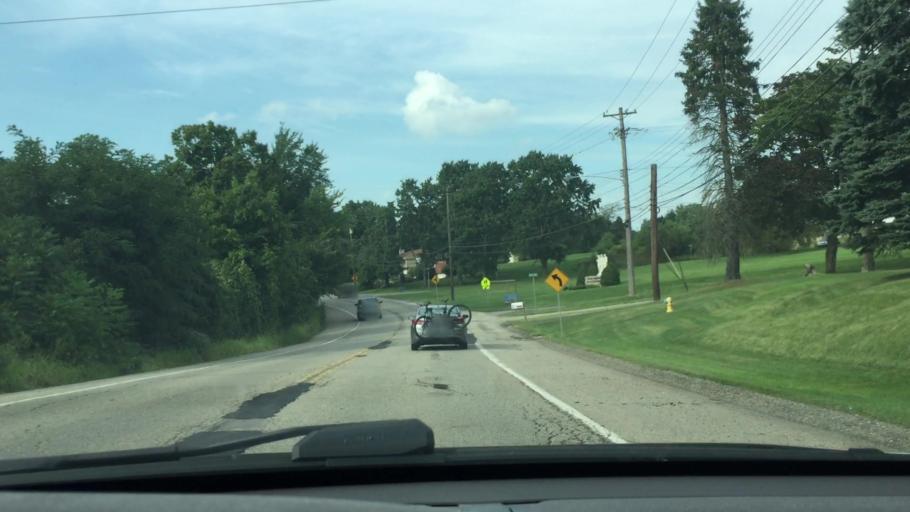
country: US
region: Pennsylvania
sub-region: Allegheny County
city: Pitcairn
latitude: 40.4243
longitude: -79.7504
